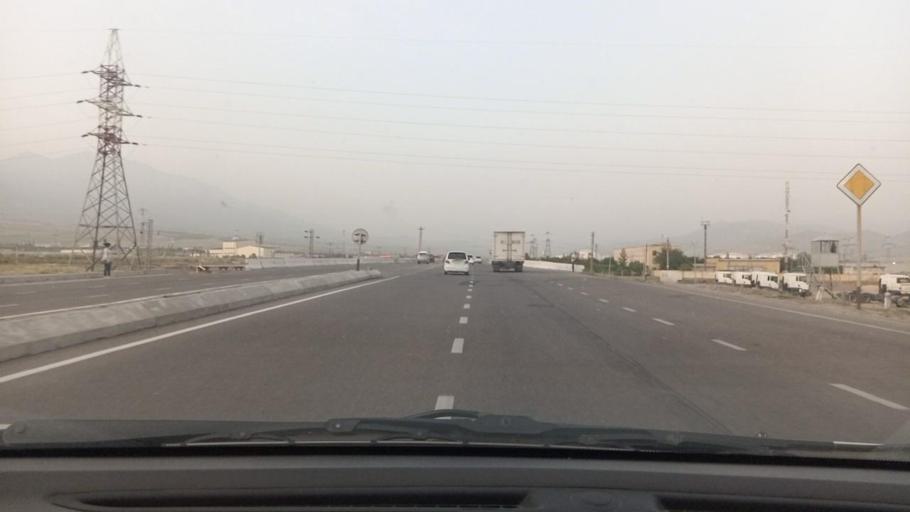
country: UZ
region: Toshkent
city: Angren
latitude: 41.0141
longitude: 70.1067
